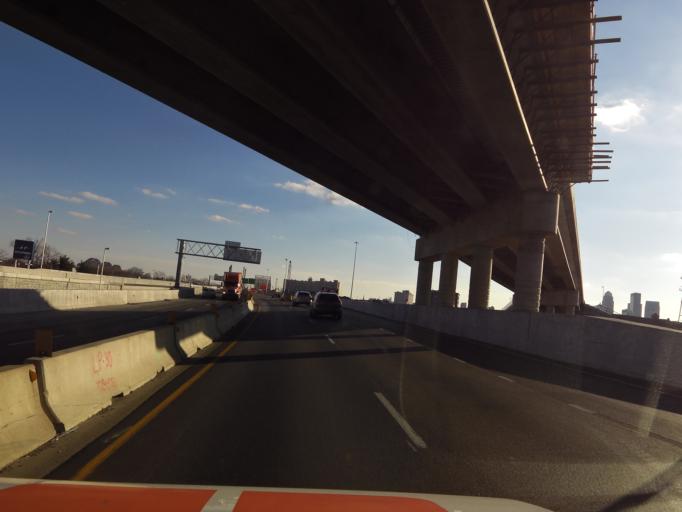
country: US
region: Indiana
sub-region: Clark County
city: Jeffersonville
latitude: 38.2754
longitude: -85.7489
